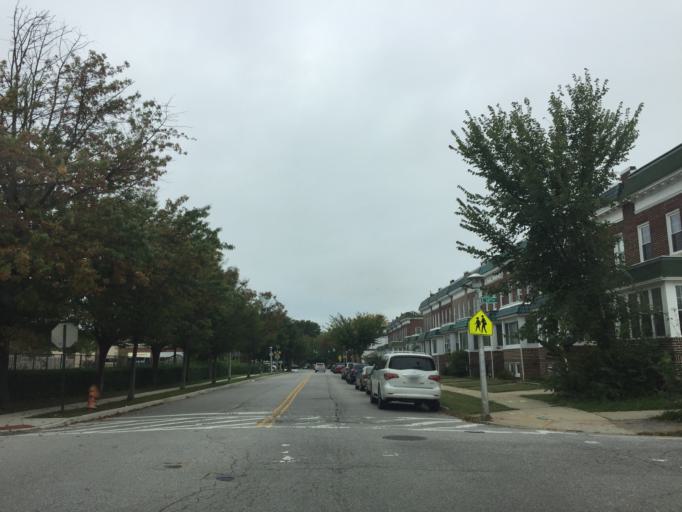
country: US
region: Maryland
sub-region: City of Baltimore
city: Baltimore
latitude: 39.3300
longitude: -76.6036
